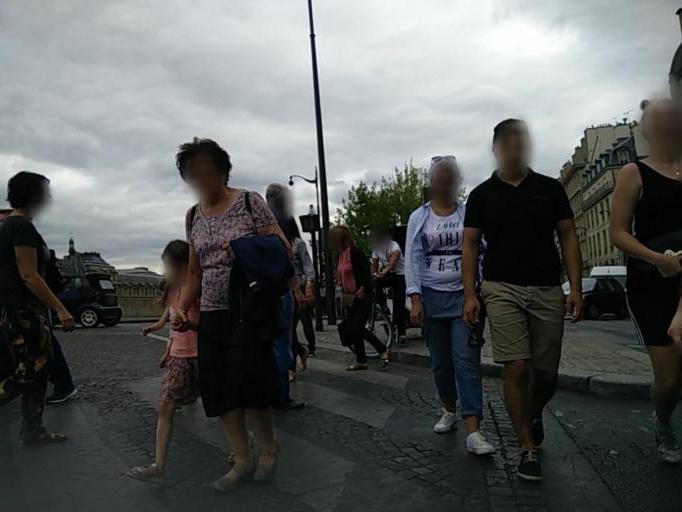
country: FR
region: Ile-de-France
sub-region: Paris
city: Paris
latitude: 48.8596
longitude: 2.3293
